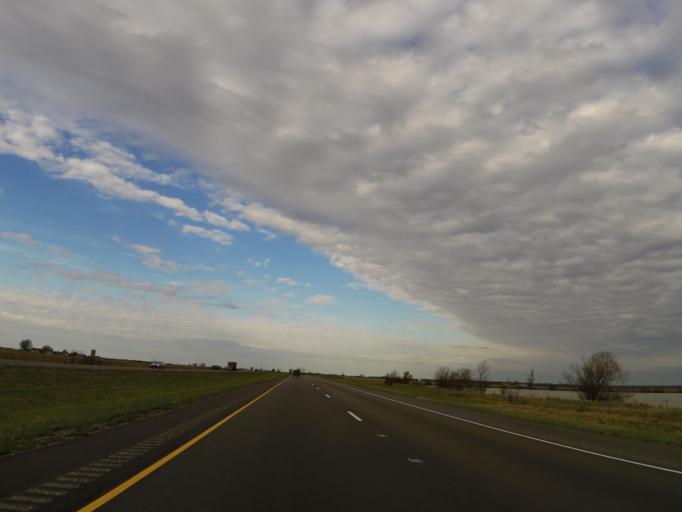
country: US
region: Illinois
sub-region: Washington County
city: Okawville
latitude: 38.4229
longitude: -89.4546
